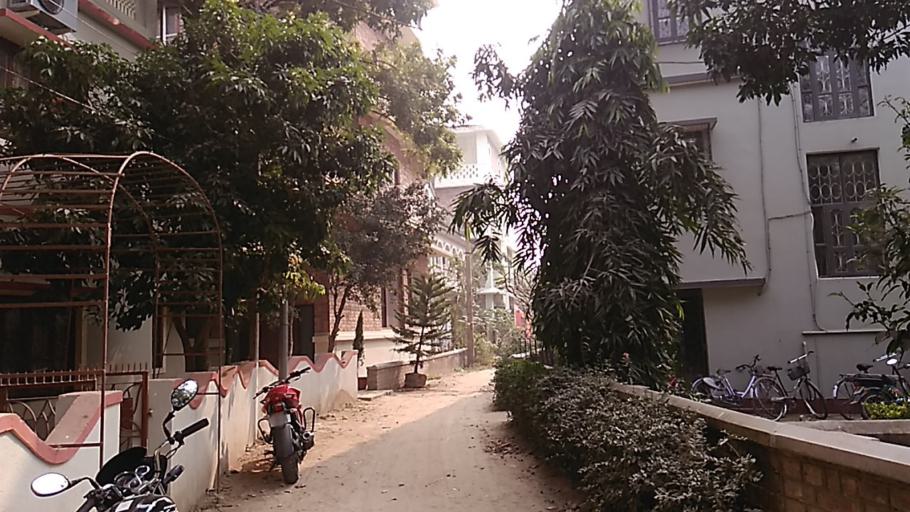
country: IN
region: West Bengal
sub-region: Nadia
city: Navadwip
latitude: 23.4162
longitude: 88.3841
